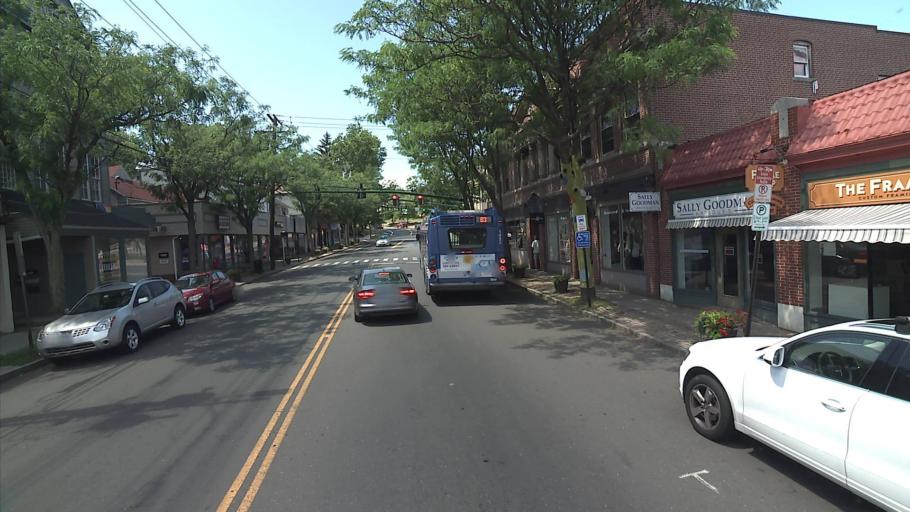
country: US
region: Connecticut
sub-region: New Haven County
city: New Haven
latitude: 41.3271
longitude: -72.9602
